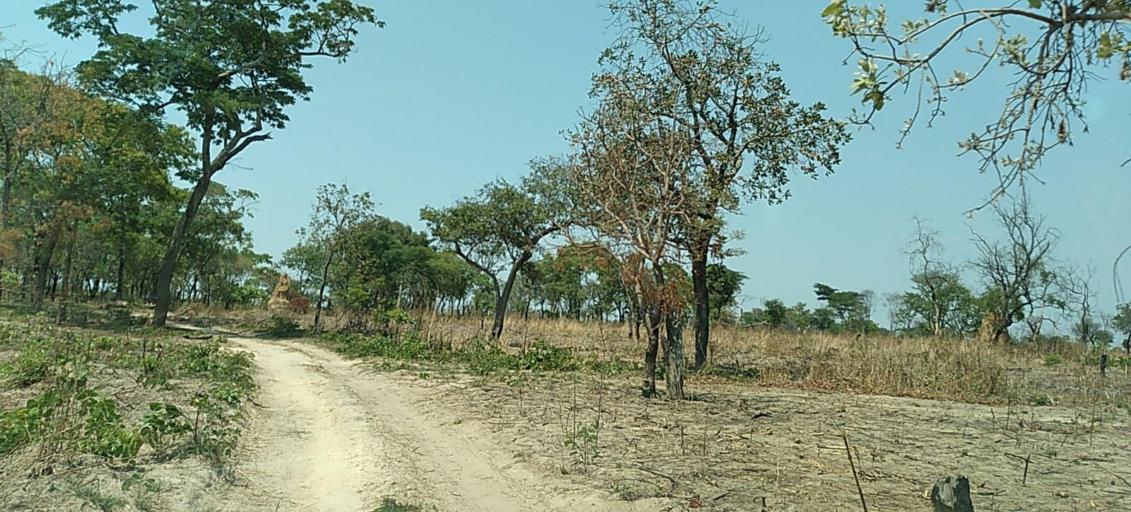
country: ZM
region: Copperbelt
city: Mpongwe
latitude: -13.8572
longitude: 28.0561
